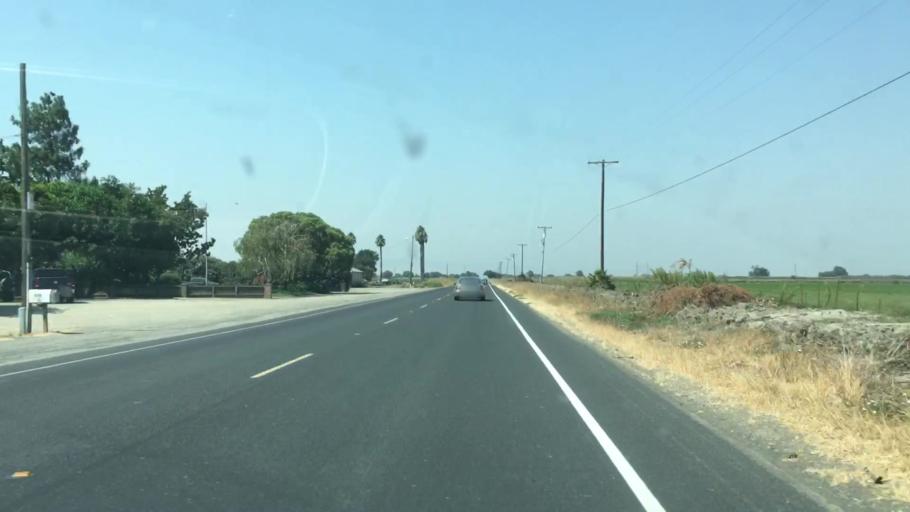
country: US
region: California
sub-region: San Joaquin County
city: Tracy
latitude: 37.8509
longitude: -121.4320
